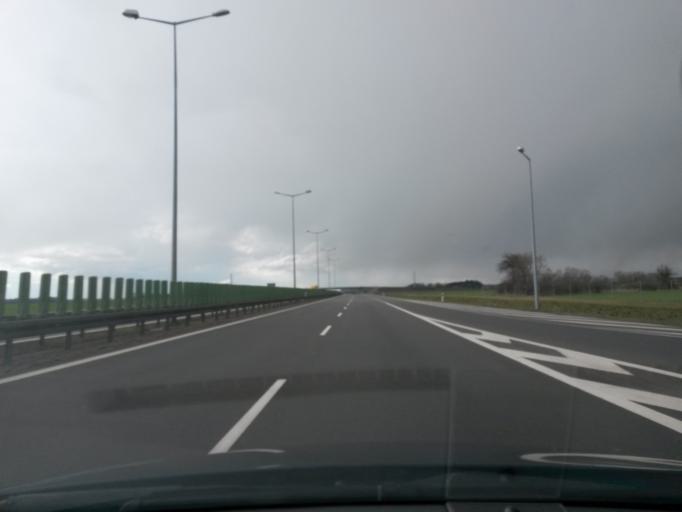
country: PL
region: Greater Poland Voivodeship
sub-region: Powiat poznanski
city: Kornik
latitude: 52.3297
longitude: 17.0883
